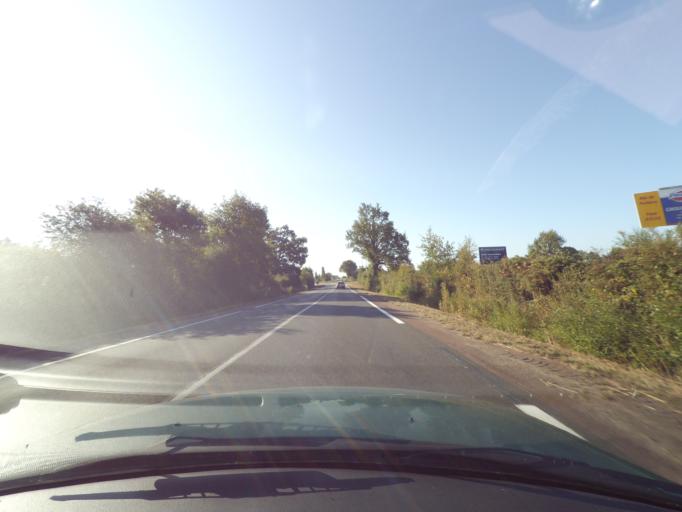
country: FR
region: Poitou-Charentes
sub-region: Departement des Deux-Sevres
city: Viennay
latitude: 46.6731
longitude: -0.2582
